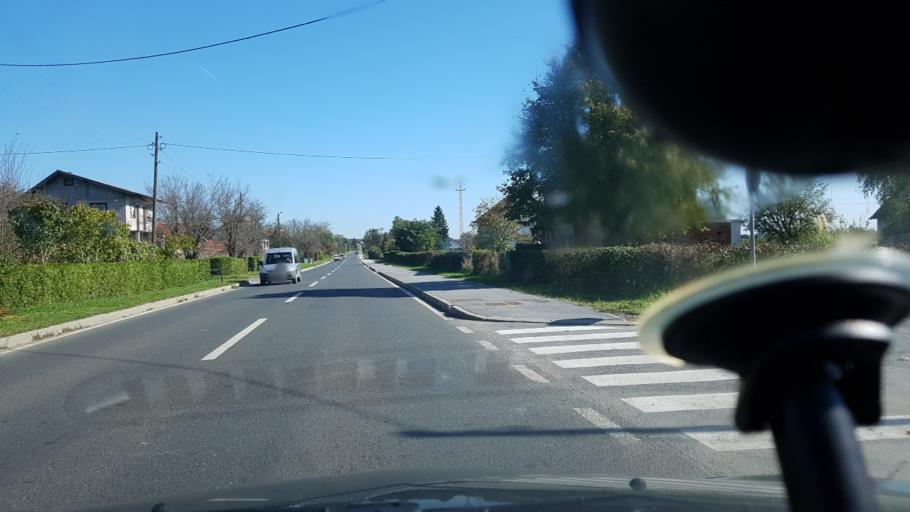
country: HR
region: Zagrebacka
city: Kriz
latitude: 45.7127
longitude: 16.4521
